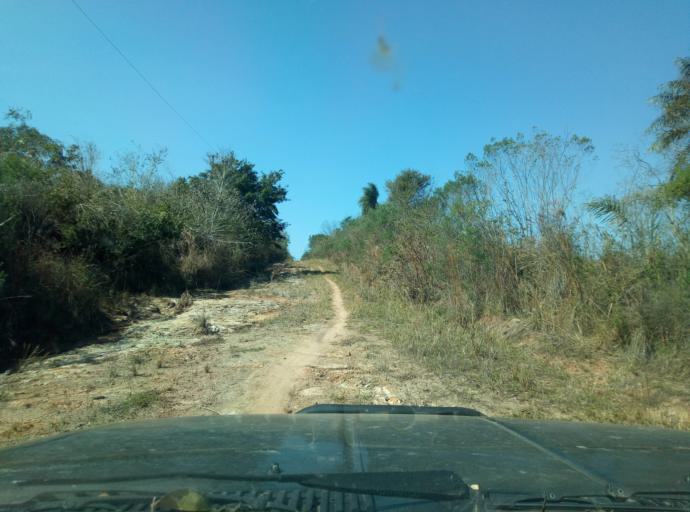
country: PY
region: Caaguazu
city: Doctor Cecilio Baez
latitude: -25.1793
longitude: -56.2216
